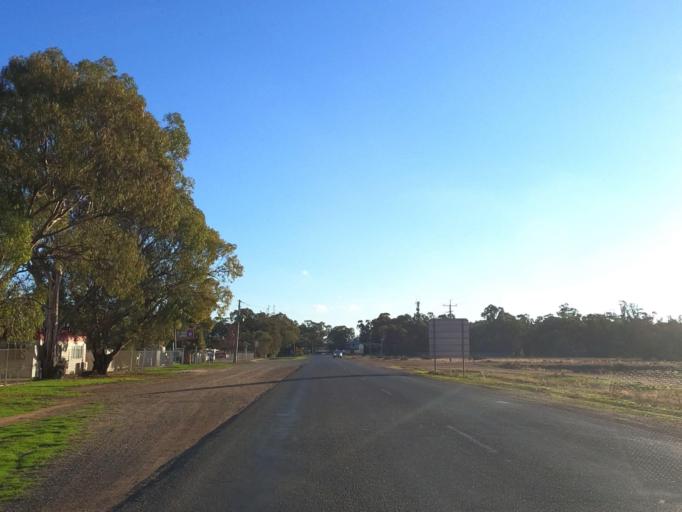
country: AU
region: Victoria
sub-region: Swan Hill
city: Swan Hill
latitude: -35.3371
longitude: 143.5687
